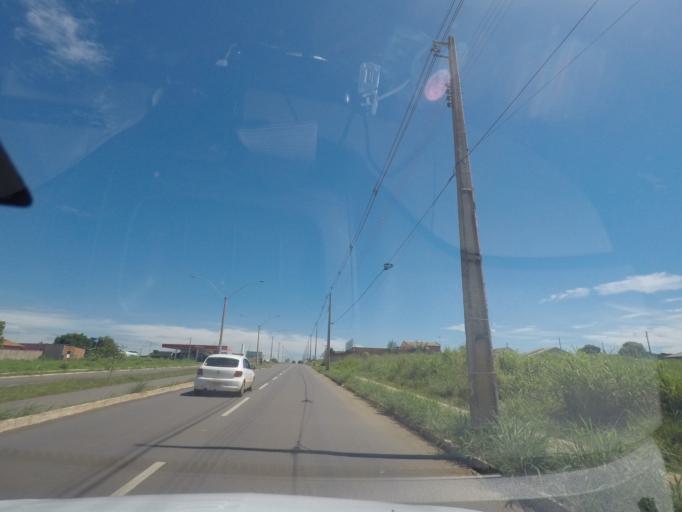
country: BR
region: Goias
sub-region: Aparecida De Goiania
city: Aparecida de Goiania
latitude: -16.7934
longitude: -49.3292
